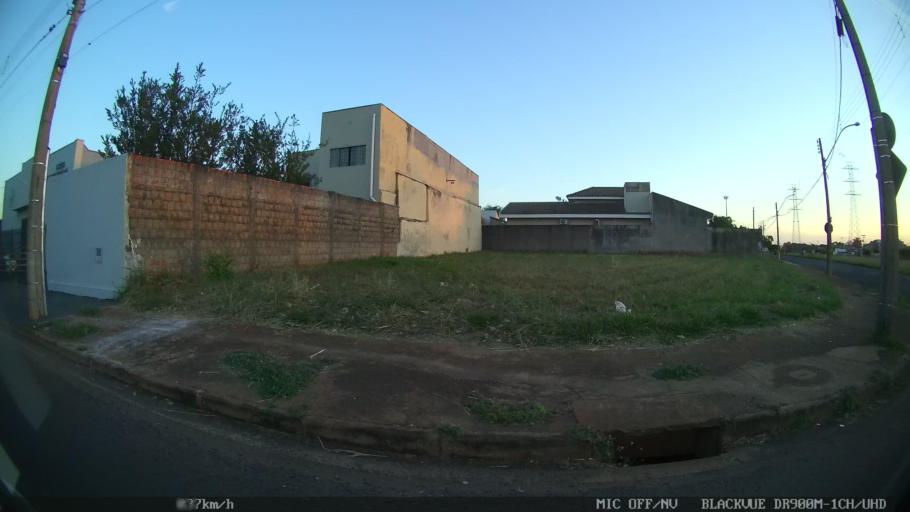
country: BR
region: Sao Paulo
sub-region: Sao Jose Do Rio Preto
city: Sao Jose do Rio Preto
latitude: -20.7962
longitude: -49.3464
